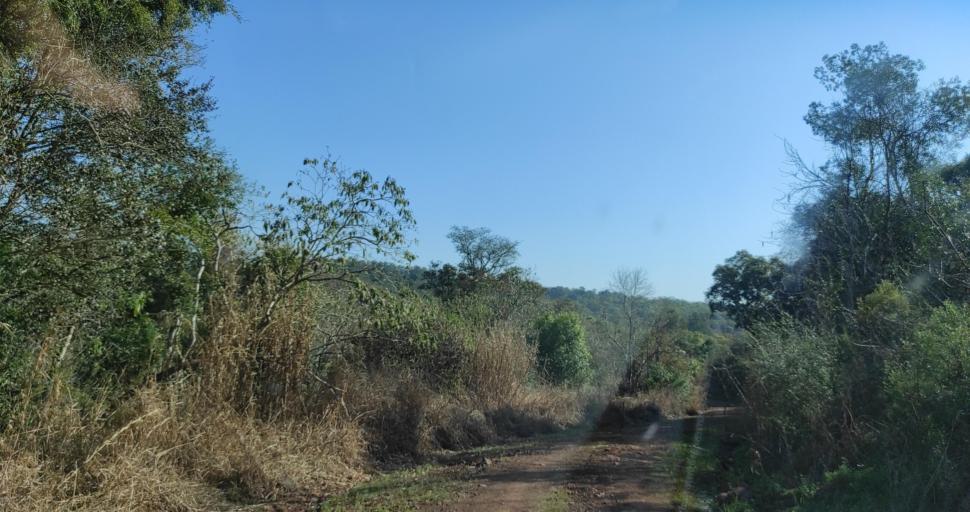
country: AR
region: Misiones
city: Capiovi
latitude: -26.9034
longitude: -55.1065
